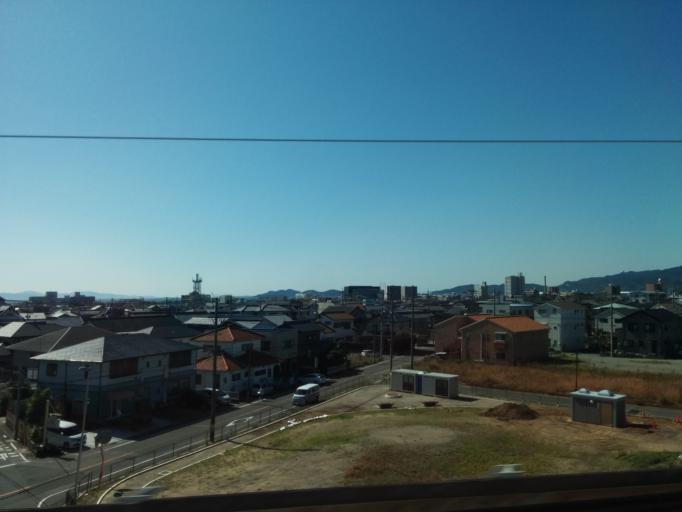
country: JP
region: Aichi
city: Gamagori
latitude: 34.8285
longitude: 137.2376
